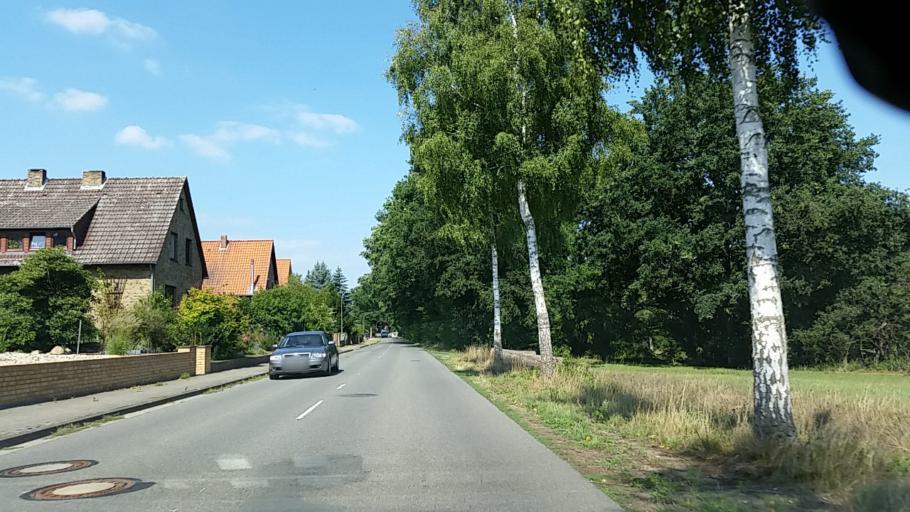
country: DE
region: Lower Saxony
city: Jelmstorf
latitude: 53.1030
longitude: 10.5486
